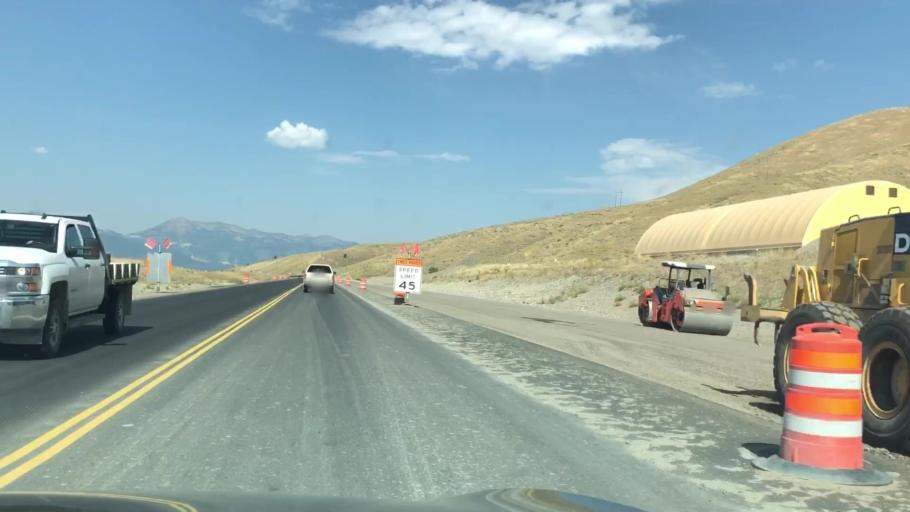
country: US
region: Wyoming
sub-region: Teton County
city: South Park
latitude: 43.4014
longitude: -110.7541
